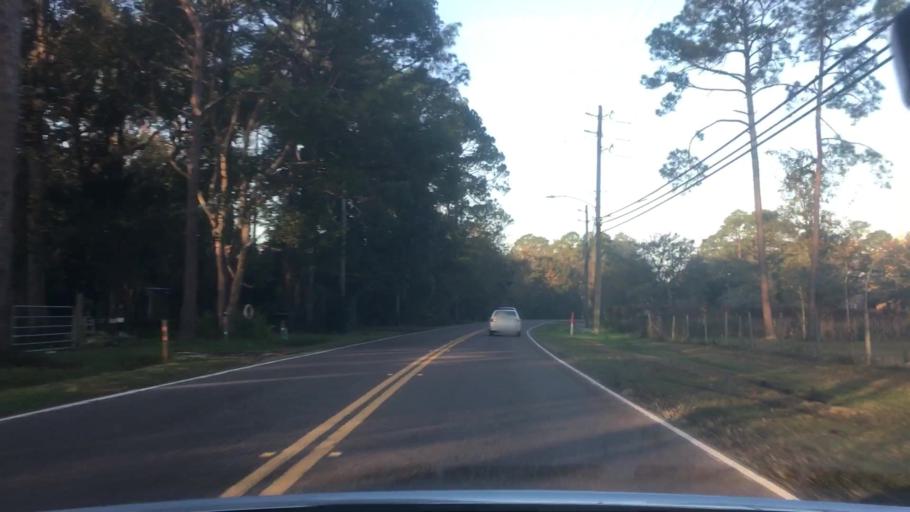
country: US
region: Florida
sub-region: Duval County
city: Jacksonville
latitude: 30.4644
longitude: -81.5913
